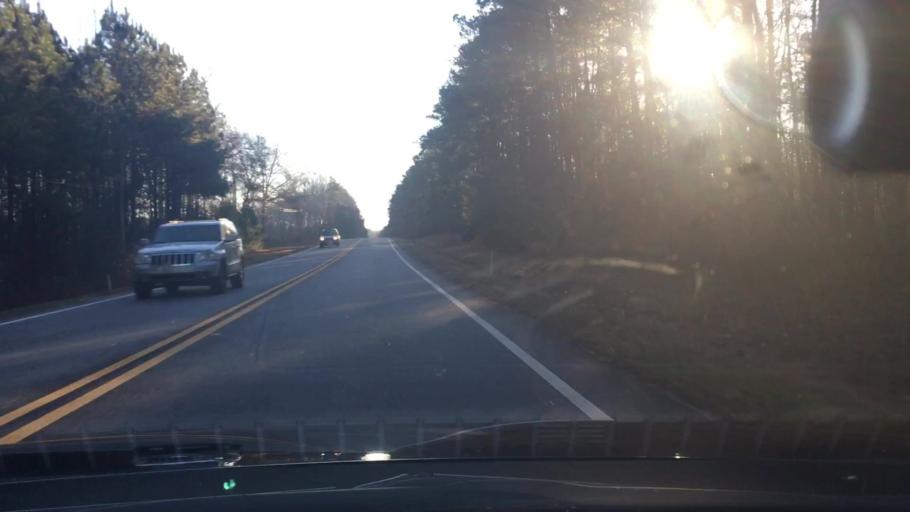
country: US
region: Georgia
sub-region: Coweta County
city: Senoia
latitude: 33.2616
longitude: -84.5141
